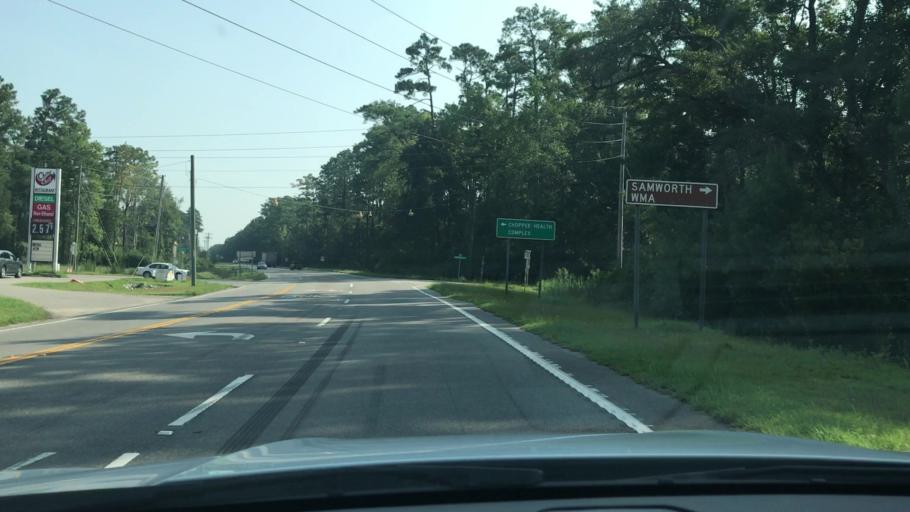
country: US
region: South Carolina
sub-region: Georgetown County
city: Georgetown
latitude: 33.4821
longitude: -79.2695
